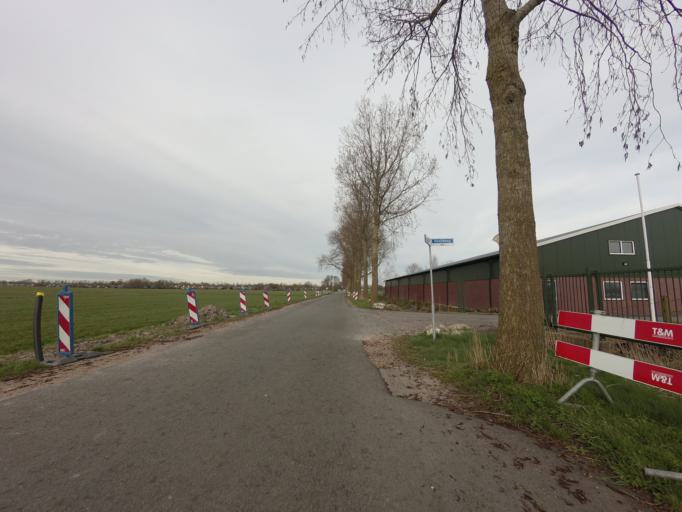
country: NL
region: Utrecht
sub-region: Gemeente De Ronde Venen
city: Mijdrecht
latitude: 52.1955
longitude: 4.8476
